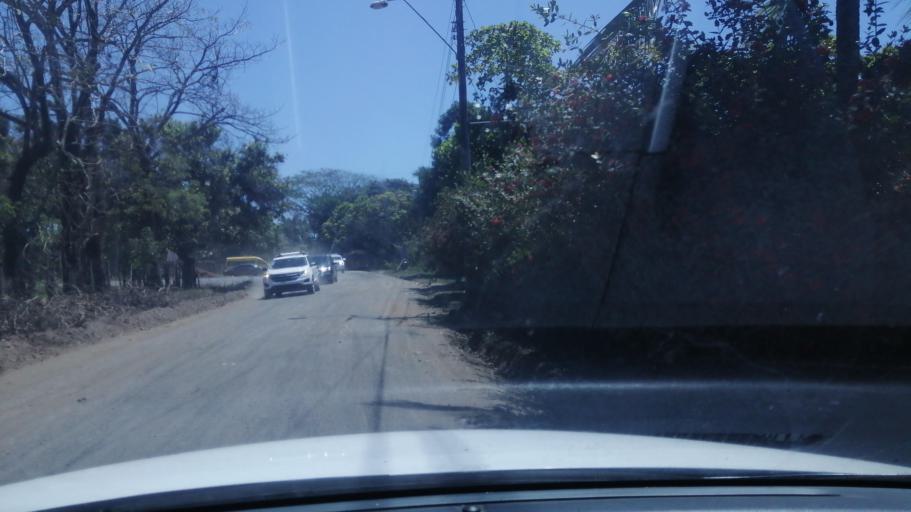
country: PA
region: Chiriqui
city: San Felix
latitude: 8.1695
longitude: -81.8656
